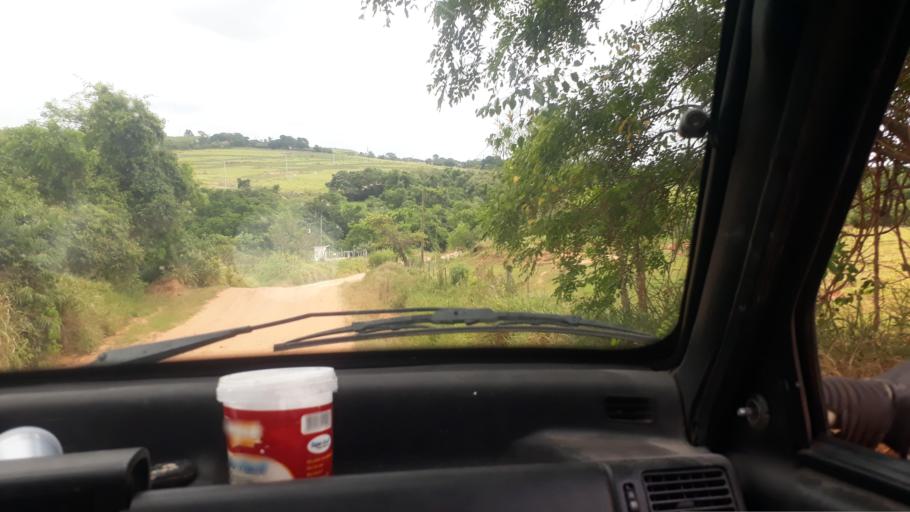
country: BR
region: Sao Paulo
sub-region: Regente Feijo
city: Regente Feijo
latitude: -22.2442
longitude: -51.2982
